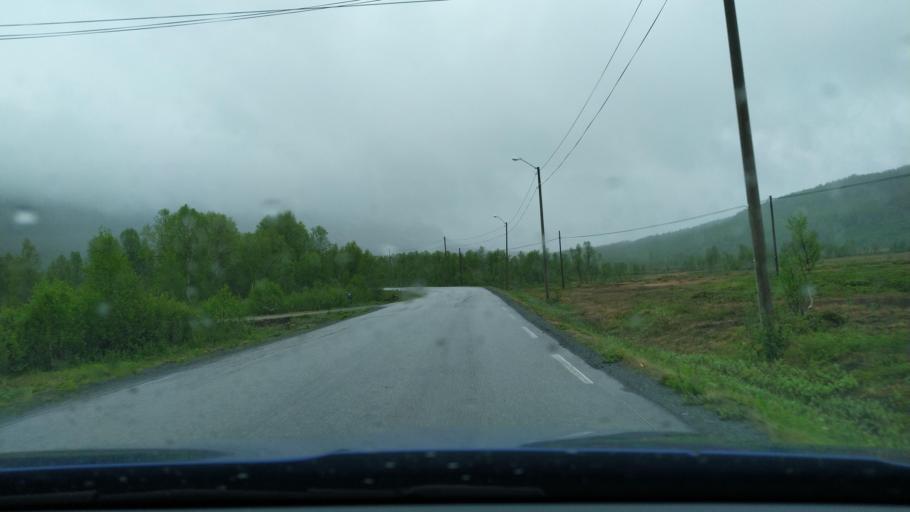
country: NO
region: Troms
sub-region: Dyroy
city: Brostadbotn
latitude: 69.0371
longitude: 17.7335
